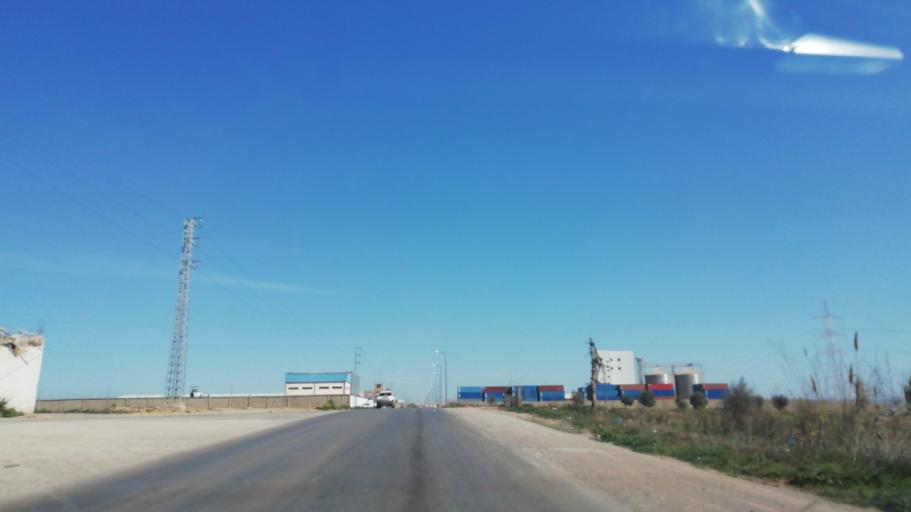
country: DZ
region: Oran
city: Es Senia
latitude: 35.5448
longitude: -0.5809
